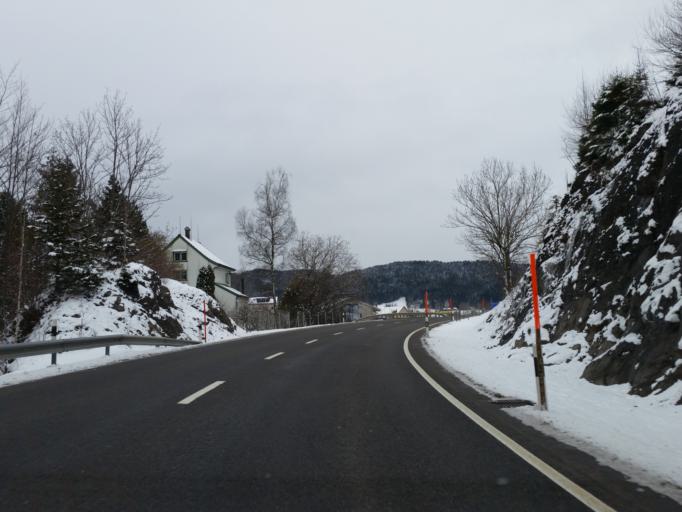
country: CH
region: Appenzell Ausserrhoden
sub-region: Bezirk Mittelland
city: Gais
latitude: 47.3608
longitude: 9.4406
